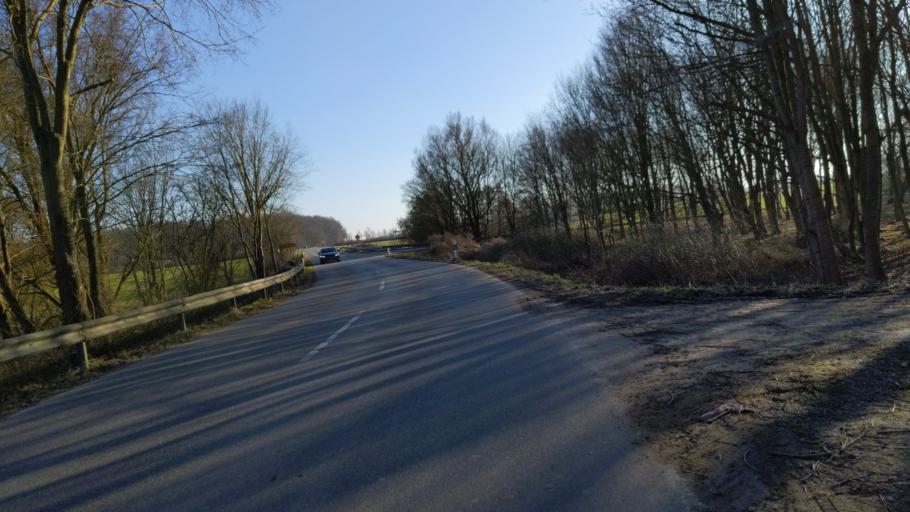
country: DE
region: Schleswig-Holstein
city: Susel
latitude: 54.0251
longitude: 10.6583
